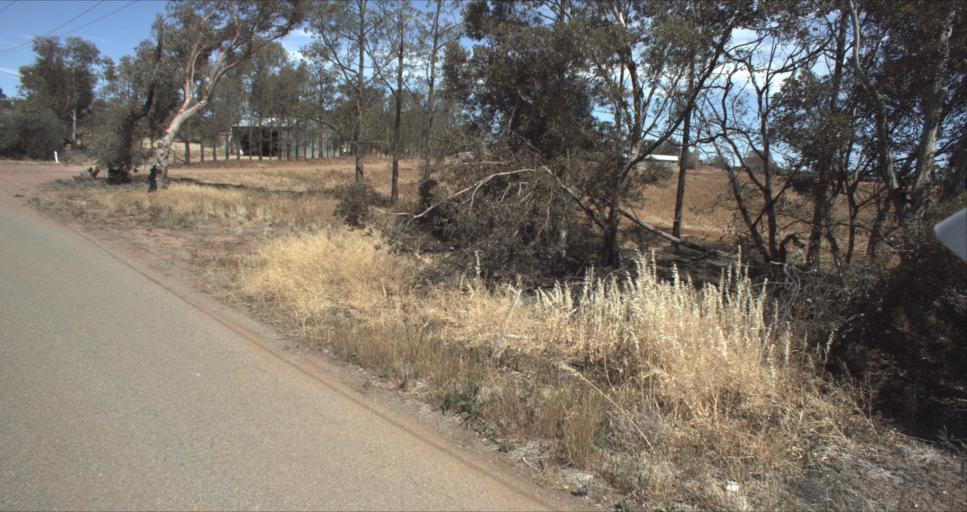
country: AU
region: New South Wales
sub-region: Leeton
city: Leeton
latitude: -34.6059
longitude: 146.4337
